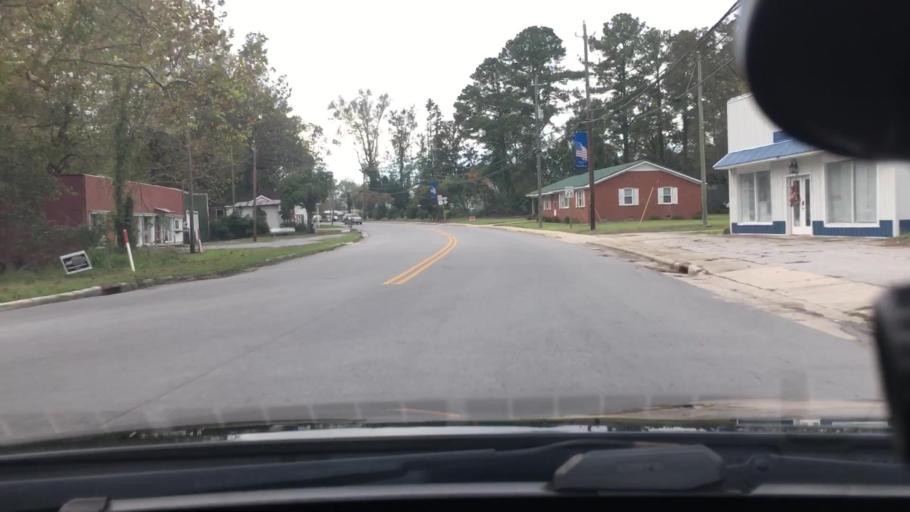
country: US
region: North Carolina
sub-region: Craven County
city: Vanceboro
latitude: 35.2972
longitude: -77.1489
